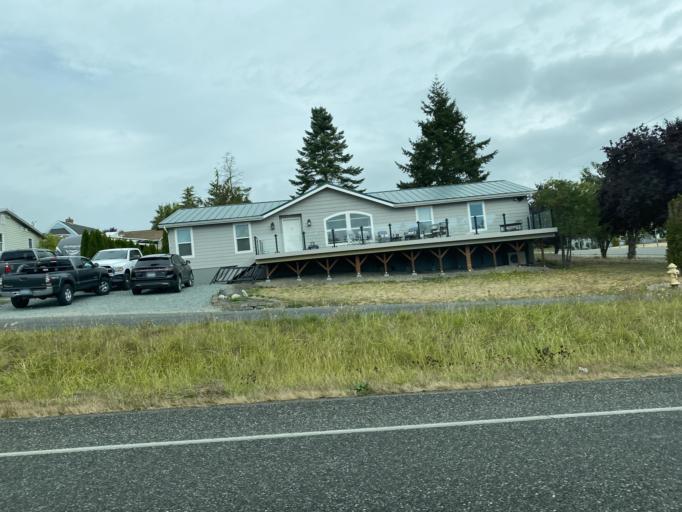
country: US
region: Washington
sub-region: Island County
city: Coupeville
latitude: 48.2408
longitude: -122.7090
